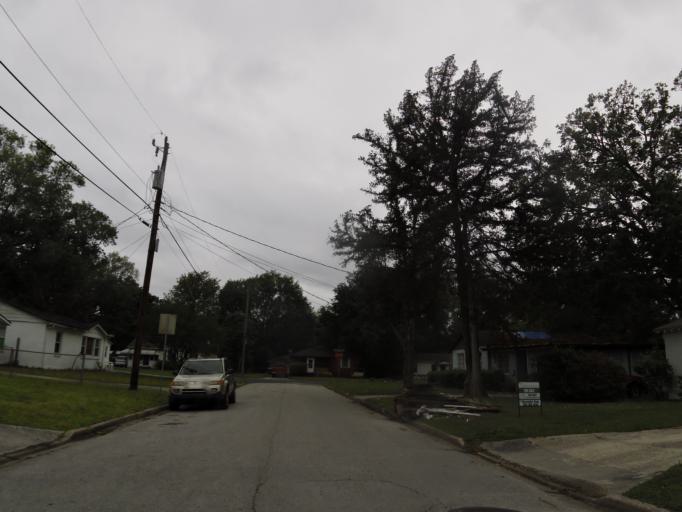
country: US
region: Florida
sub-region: Duval County
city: Jacksonville
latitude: 30.2978
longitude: -81.6280
